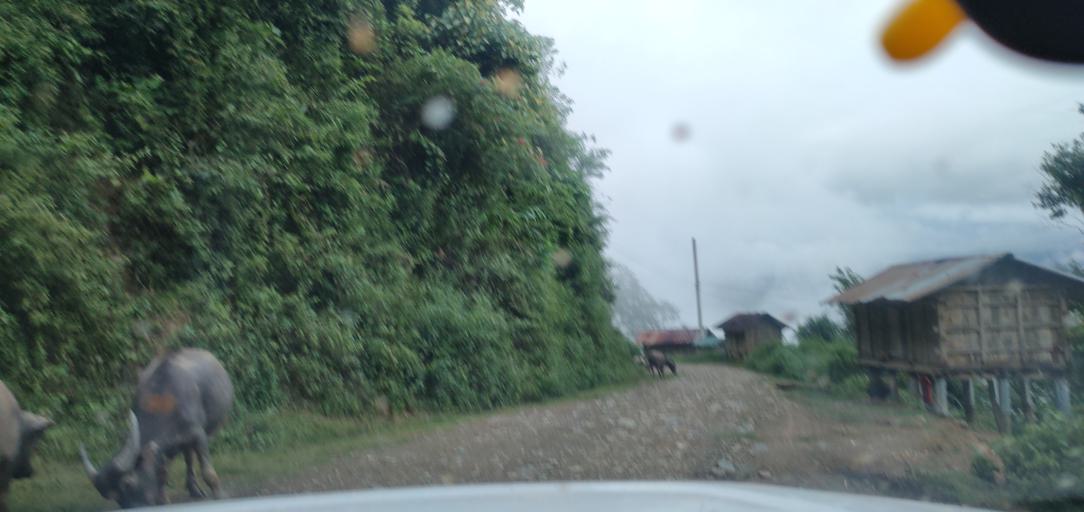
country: LA
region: Phongsali
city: Phongsali
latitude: 21.4449
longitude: 102.2973
